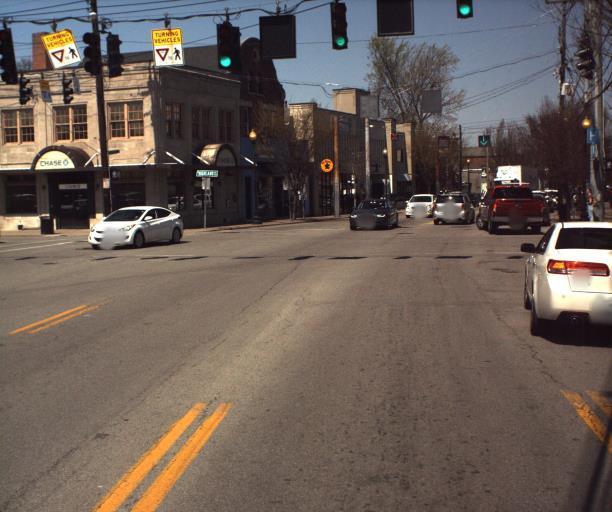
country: US
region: Kentucky
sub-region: Jefferson County
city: Audubon Park
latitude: 38.2401
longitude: -85.7240
